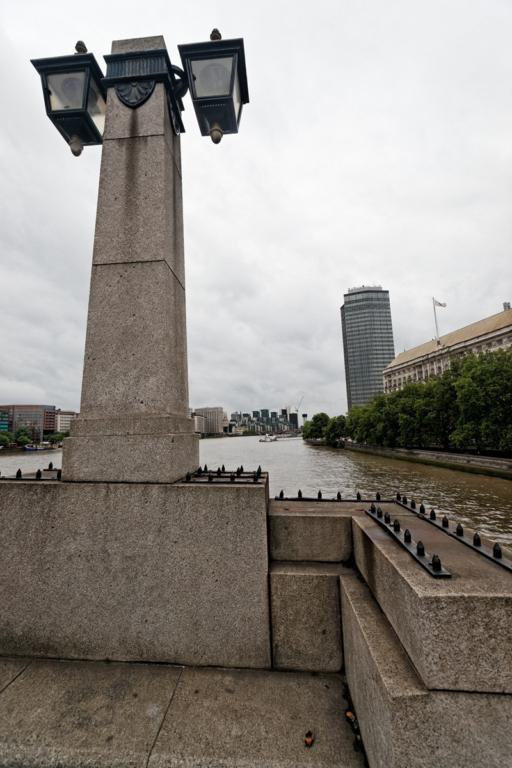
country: GB
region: England
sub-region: Greater London
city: City of Westminster
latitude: 51.4946
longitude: -0.1242
